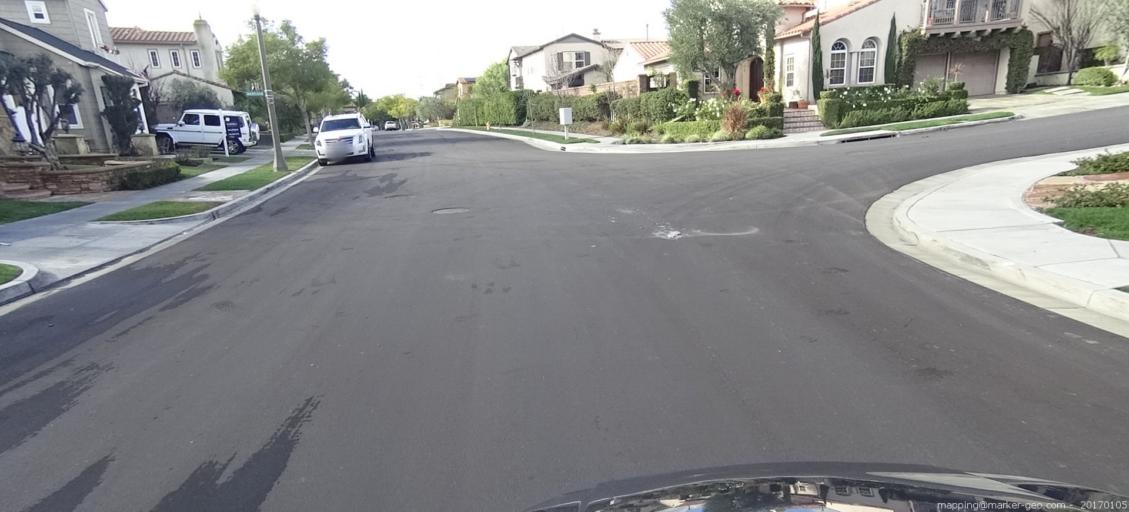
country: US
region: California
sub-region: Orange County
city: Ladera Ranch
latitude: 33.5584
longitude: -117.6375
